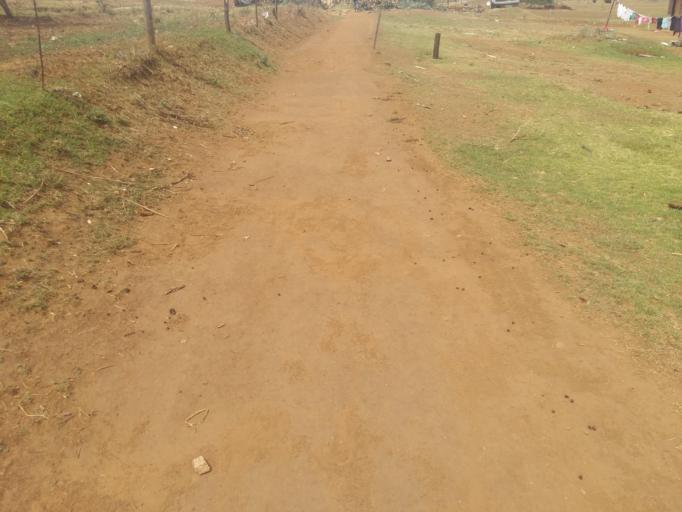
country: LS
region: Mafeteng
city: Mafeteng
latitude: -29.7028
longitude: 27.4336
